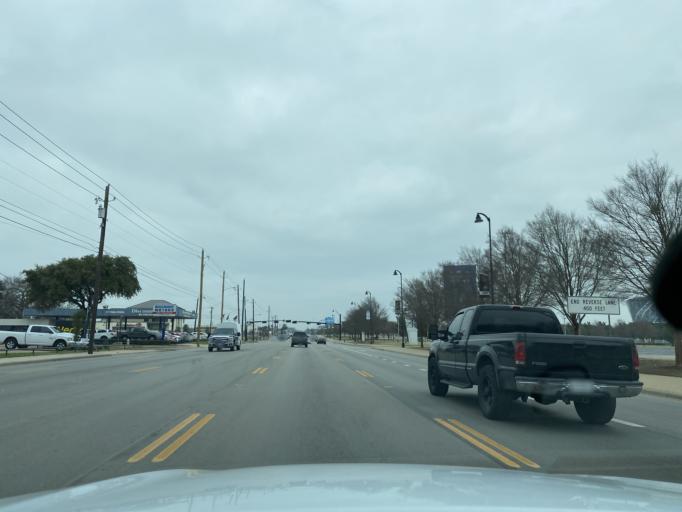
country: US
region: Texas
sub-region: Tarrant County
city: Arlington
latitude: 32.7444
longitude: -97.0973
